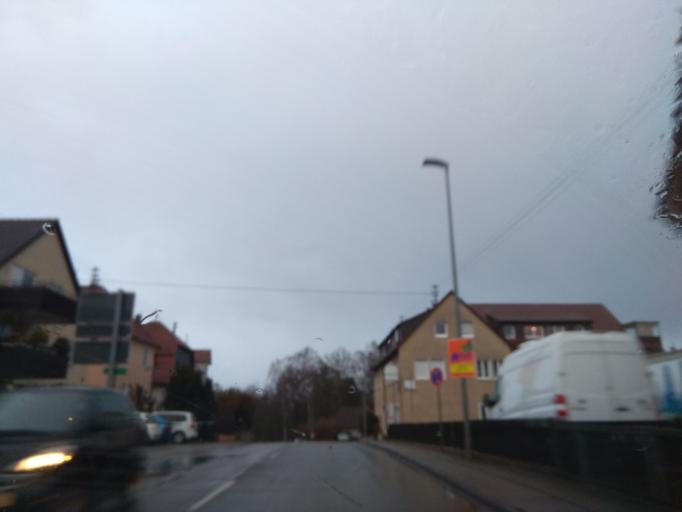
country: DE
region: Baden-Wuerttemberg
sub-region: Regierungsbezirk Stuttgart
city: Steinenbronn
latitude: 48.6918
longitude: 9.1264
